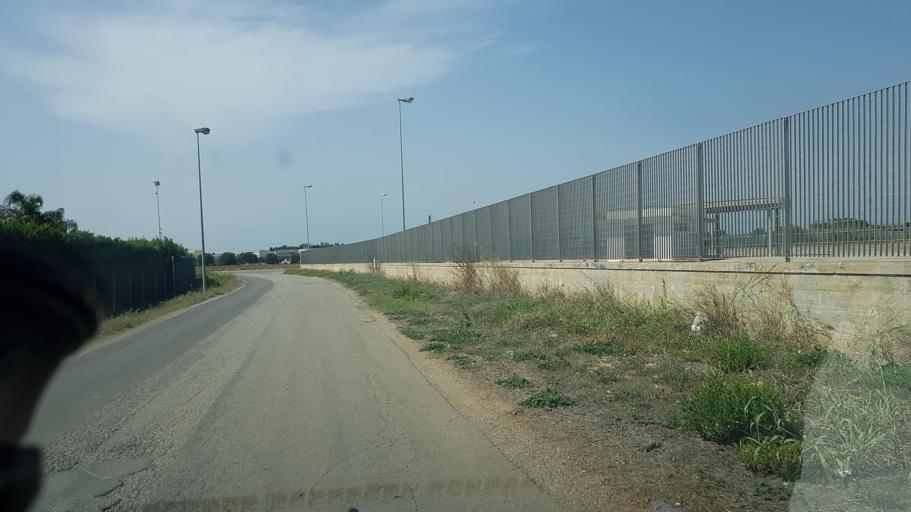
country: IT
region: Apulia
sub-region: Provincia di Brindisi
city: Mesagne
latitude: 40.5667
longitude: 17.8254
